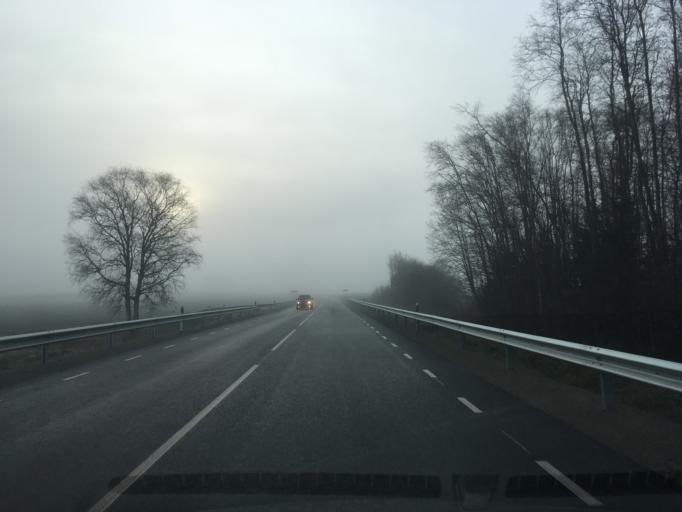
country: EE
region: Harju
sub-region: Anija vald
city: Kehra
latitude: 59.3903
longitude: 25.2876
